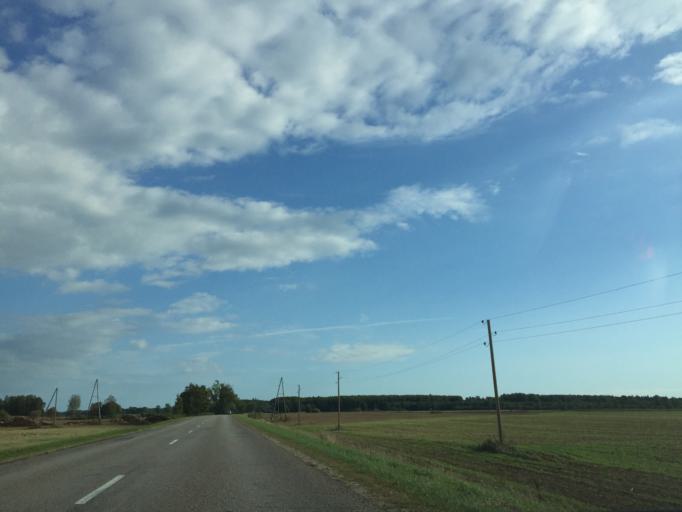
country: LV
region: Limbazu Rajons
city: Limbazi
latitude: 57.5082
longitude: 24.5066
